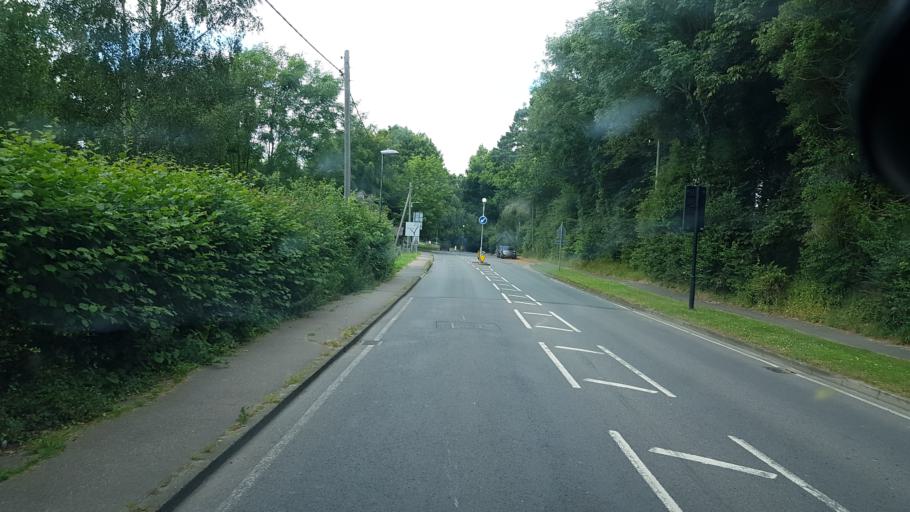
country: GB
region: England
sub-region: West Sussex
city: South Nutfield
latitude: 51.0613
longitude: -0.1357
